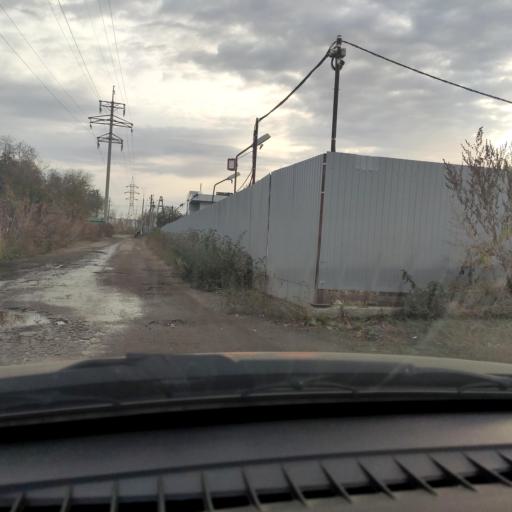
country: RU
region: Samara
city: Tol'yatti
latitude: 53.5507
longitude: 49.3001
